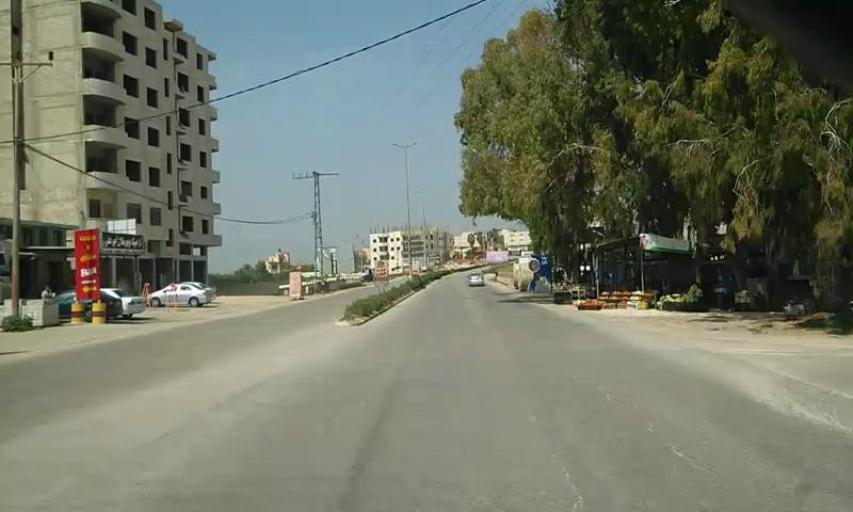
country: PS
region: West Bank
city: Janin
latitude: 32.4798
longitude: 35.2997
